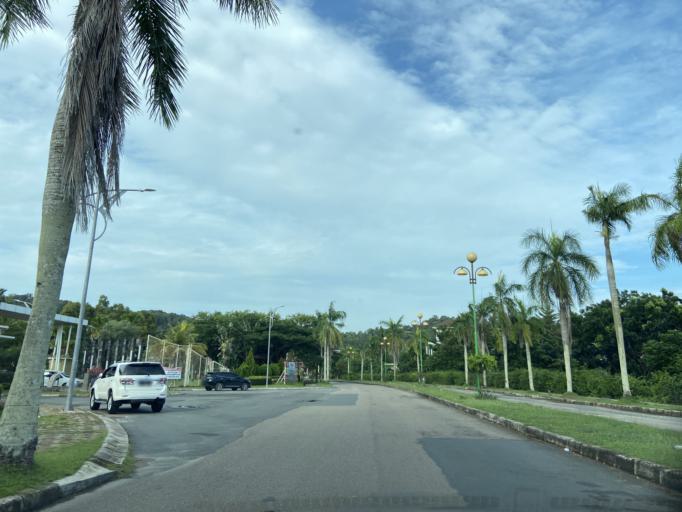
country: SG
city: Singapore
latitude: 1.1057
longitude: 104.0273
